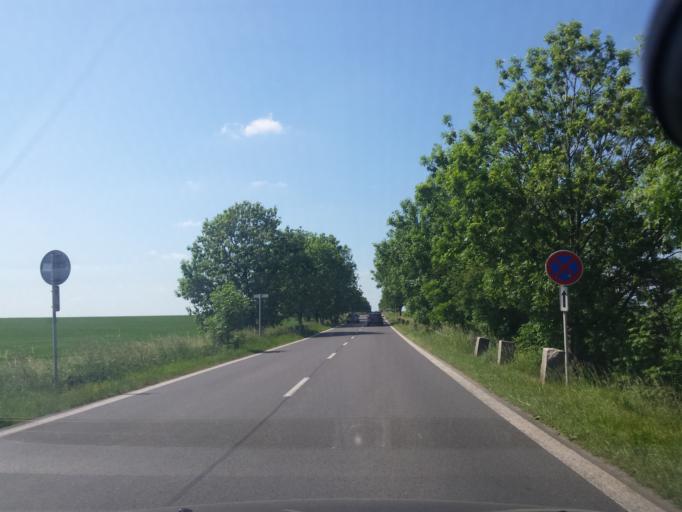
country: CZ
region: Central Bohemia
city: Horomerice
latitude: 50.1233
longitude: 14.3522
